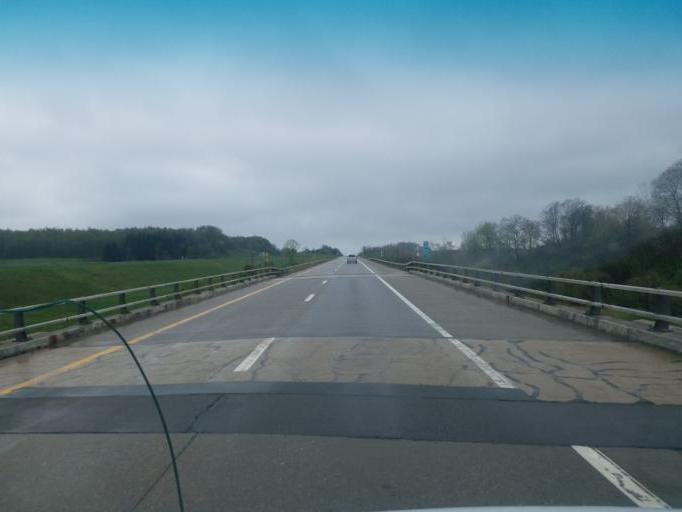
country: US
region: New York
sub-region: Chautauqua County
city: Clymer
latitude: 42.1468
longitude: -79.6125
